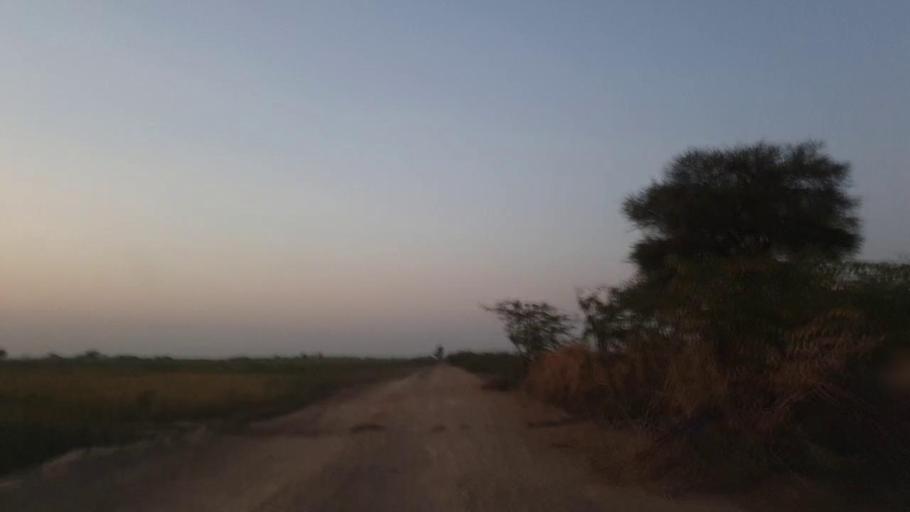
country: PK
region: Sindh
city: Naukot
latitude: 24.8964
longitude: 69.3820
